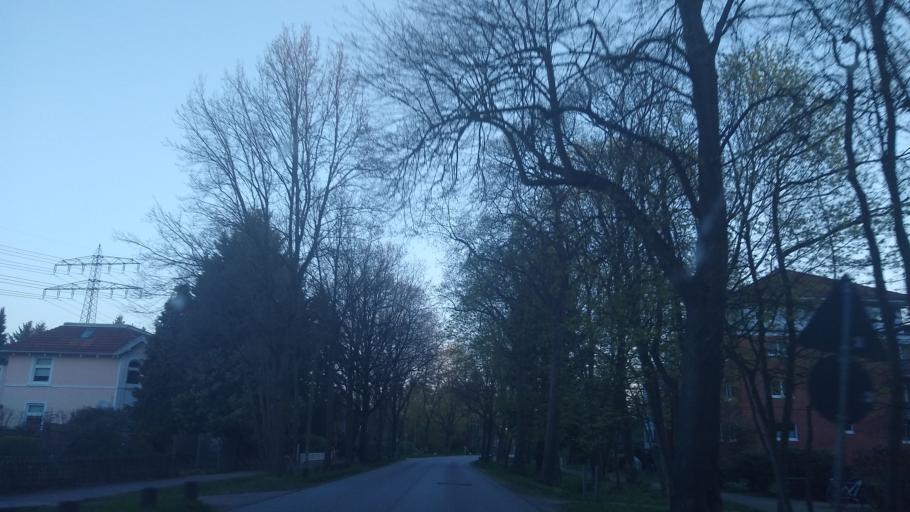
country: DE
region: Schleswig-Holstein
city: Bonningstedt
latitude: 53.6484
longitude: 9.9074
